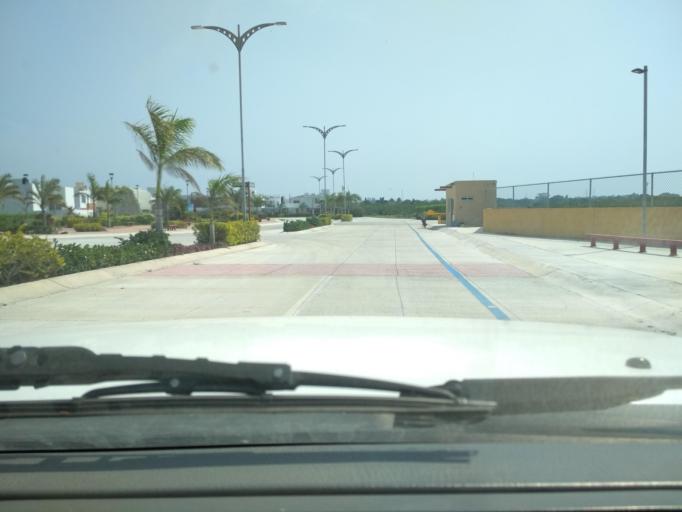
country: MX
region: Veracruz
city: Boca del Rio
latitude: 19.1065
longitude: -96.1261
